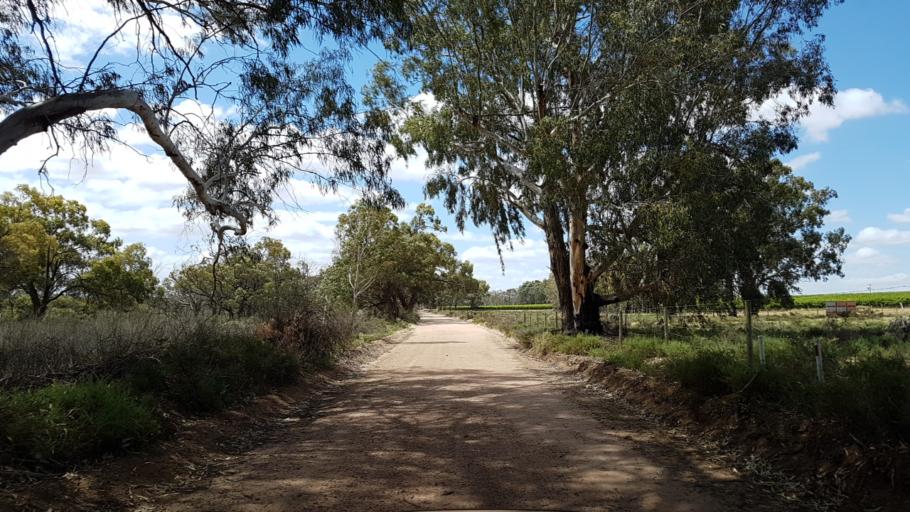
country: AU
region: South Australia
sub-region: Loxton Waikerie
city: Waikerie
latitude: -34.1731
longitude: 140.0228
